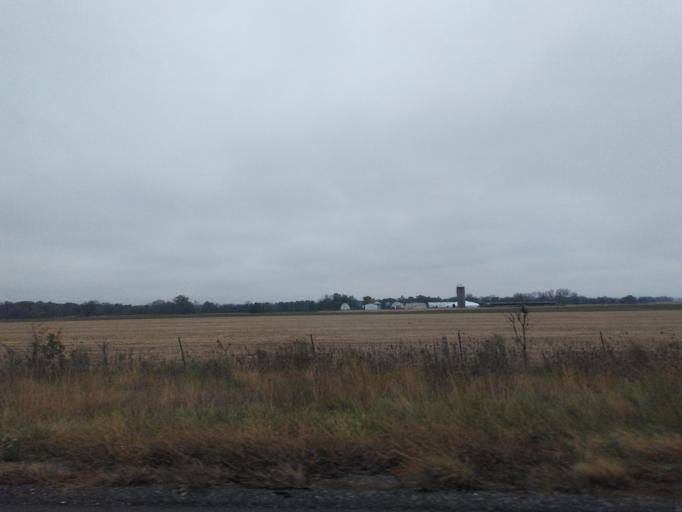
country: US
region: Illinois
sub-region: Madison County
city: Highland
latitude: 38.7867
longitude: -89.6400
